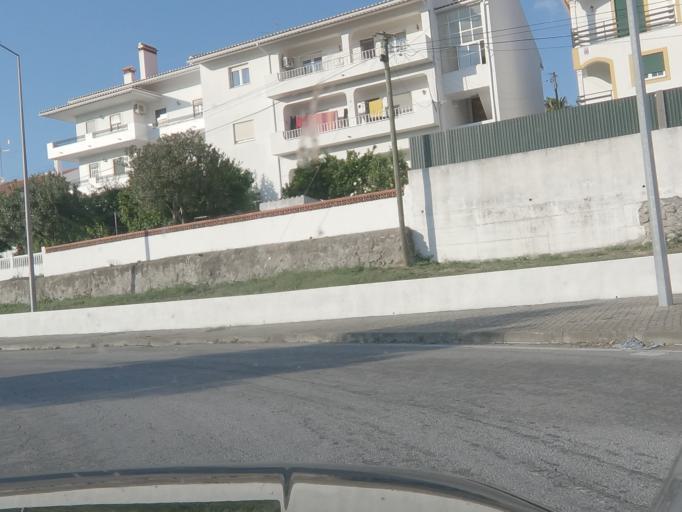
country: PT
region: Portalegre
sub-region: Portalegre
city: Portalegre
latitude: 39.3106
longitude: -7.4405
